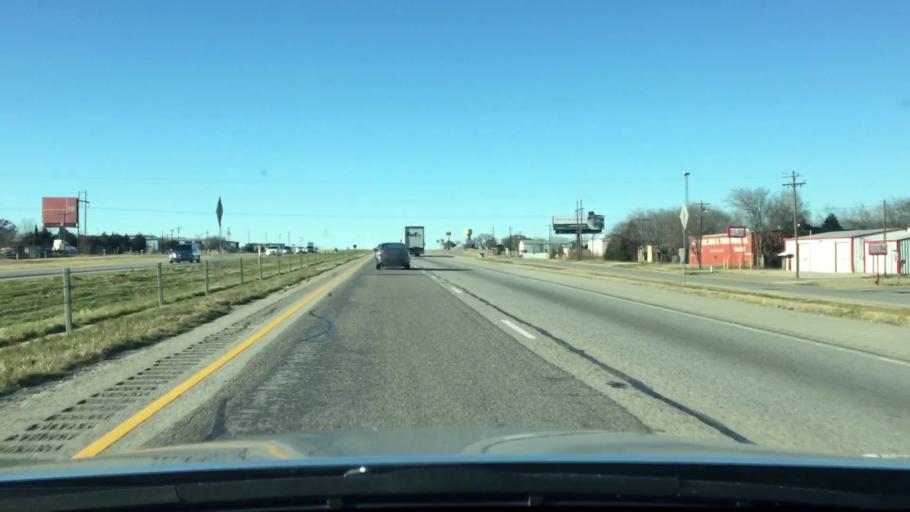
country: US
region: Texas
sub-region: Johnson County
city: Alvarado
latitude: 32.4549
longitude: -97.2598
